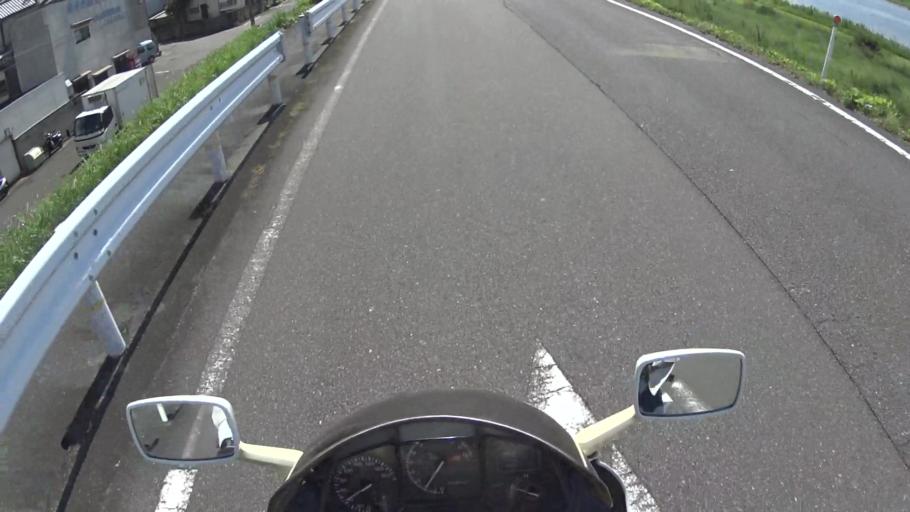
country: JP
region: Kyoto
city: Muko
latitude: 34.9987
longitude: 135.7082
